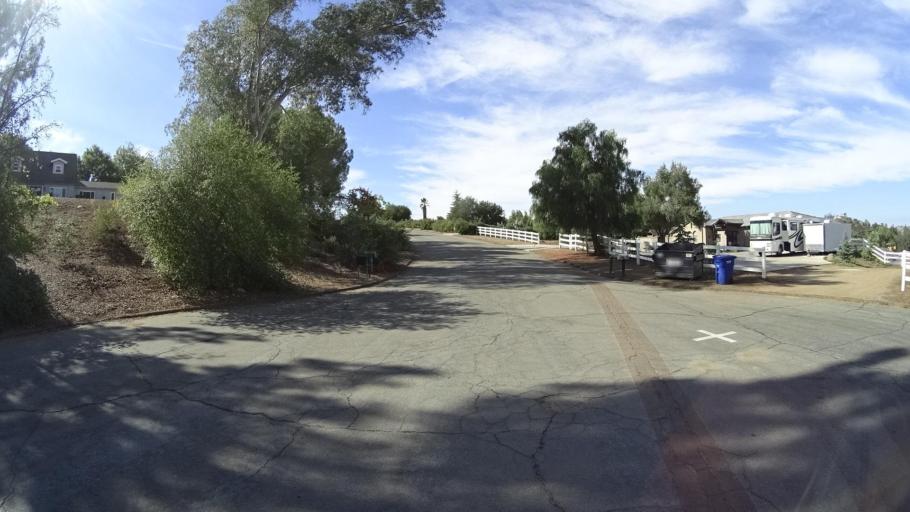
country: US
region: California
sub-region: San Diego County
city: Alpine
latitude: 32.8257
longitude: -116.7818
